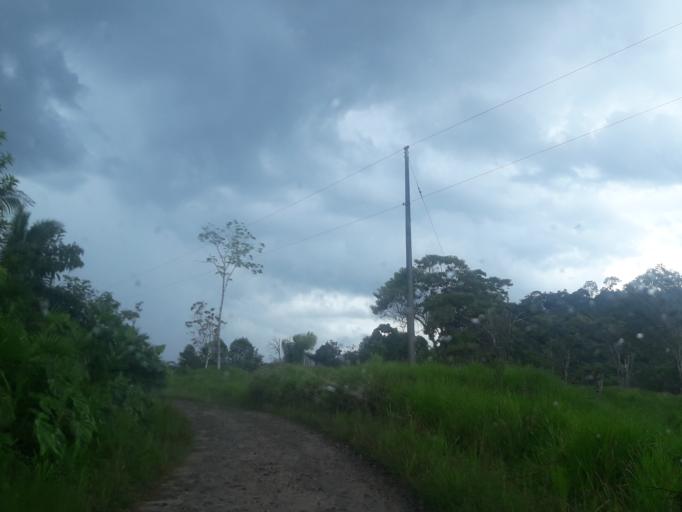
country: EC
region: Napo
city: Tena
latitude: -1.0854
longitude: -77.7087
